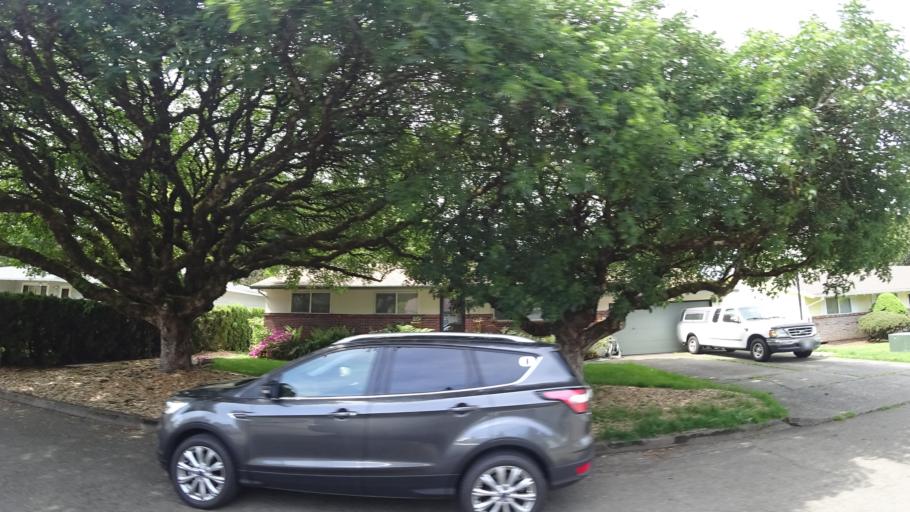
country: US
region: Oregon
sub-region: Clackamas County
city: Milwaukie
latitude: 45.4496
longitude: -122.6126
